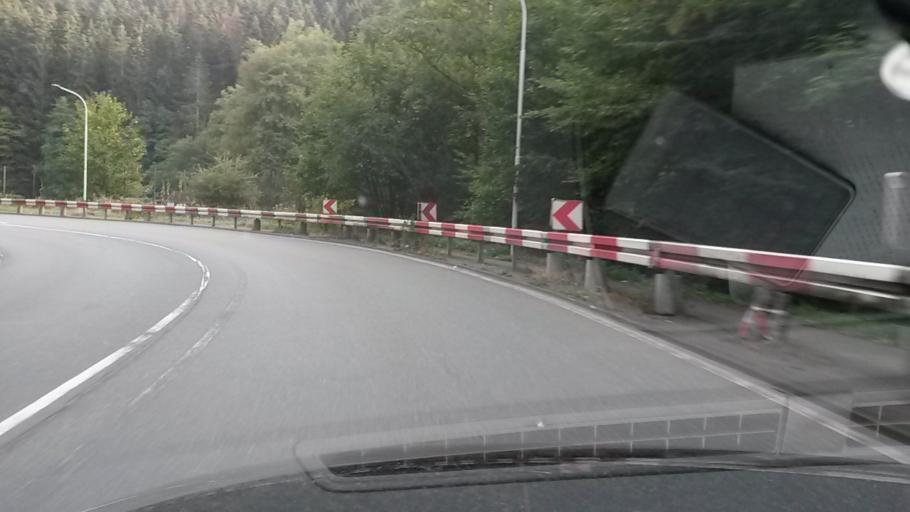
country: DE
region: North Rhine-Westphalia
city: Werdohl
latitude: 51.2300
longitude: 7.7212
